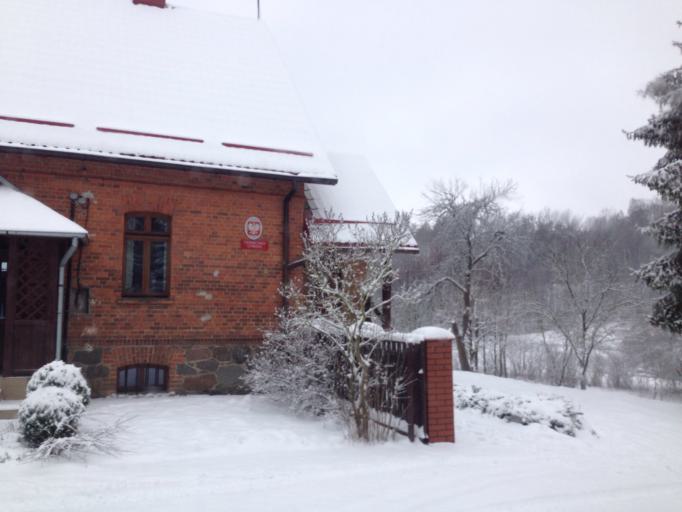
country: PL
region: Kujawsko-Pomorskie
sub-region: Powiat brodnicki
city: Gorzno
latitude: 53.1864
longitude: 19.6632
